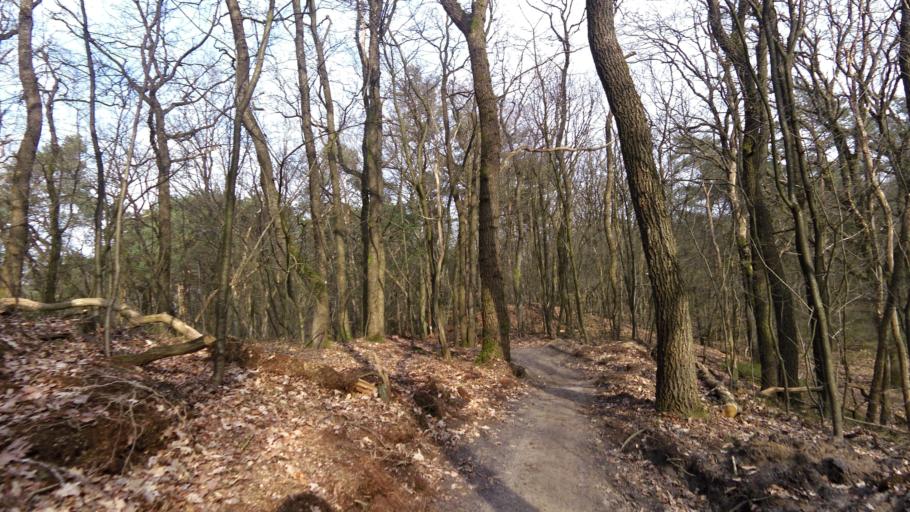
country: NL
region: Gelderland
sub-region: Gemeente Ede
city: Otterlo
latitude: 52.0913
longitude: 5.7878
